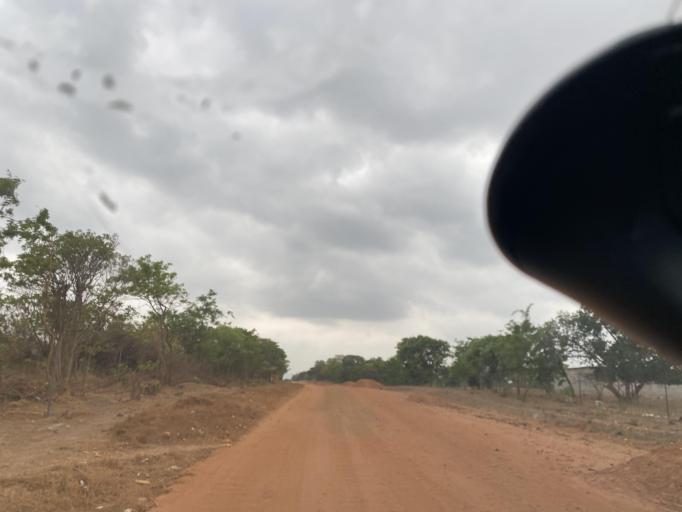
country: ZM
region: Lusaka
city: Chongwe
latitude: -15.2747
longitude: 28.7308
